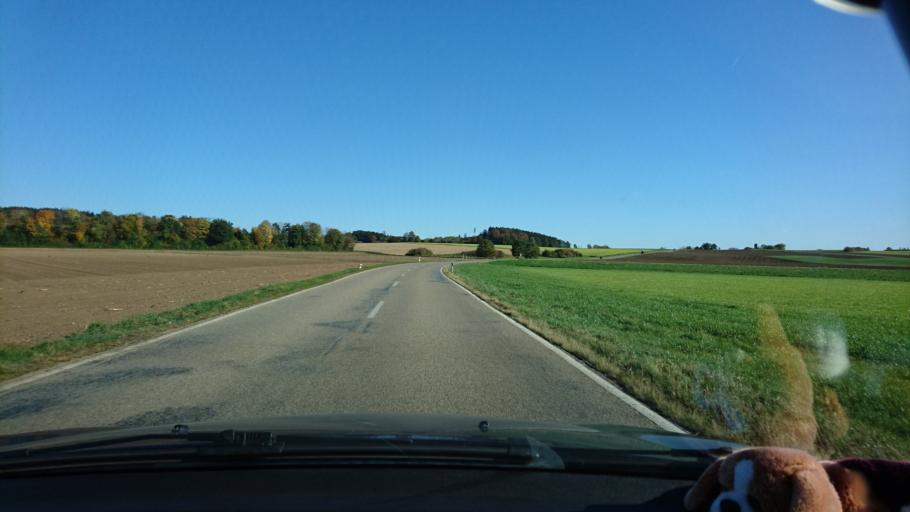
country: DE
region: Bavaria
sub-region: Upper Bavaria
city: Poing
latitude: 48.1399
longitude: 11.8240
